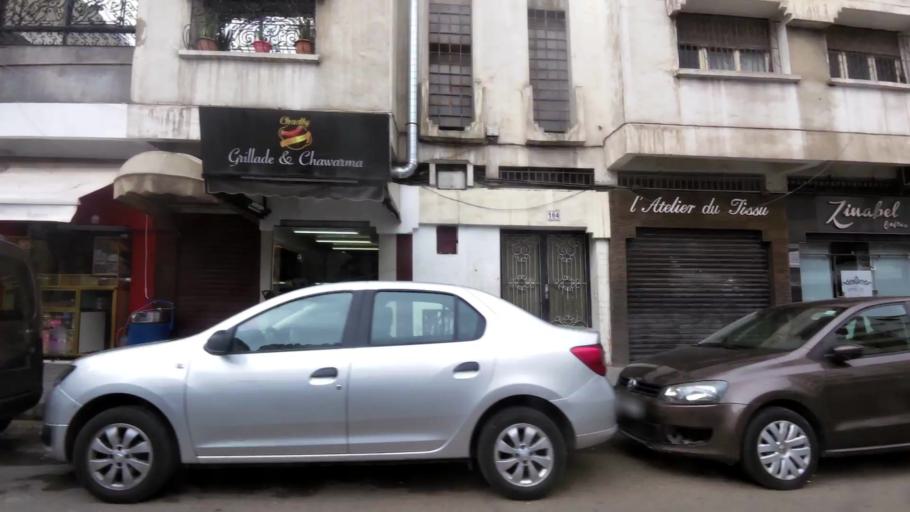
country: MA
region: Grand Casablanca
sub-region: Casablanca
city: Casablanca
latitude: 33.5977
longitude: -7.6450
